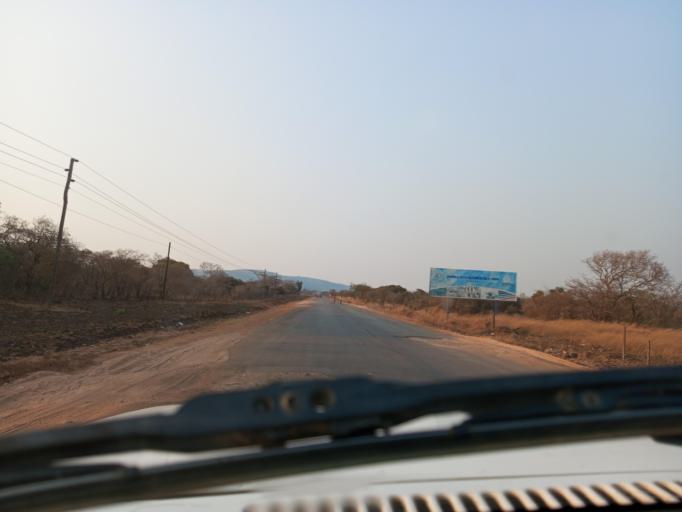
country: ZM
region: Northern
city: Mpika
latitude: -11.9205
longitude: 31.4167
